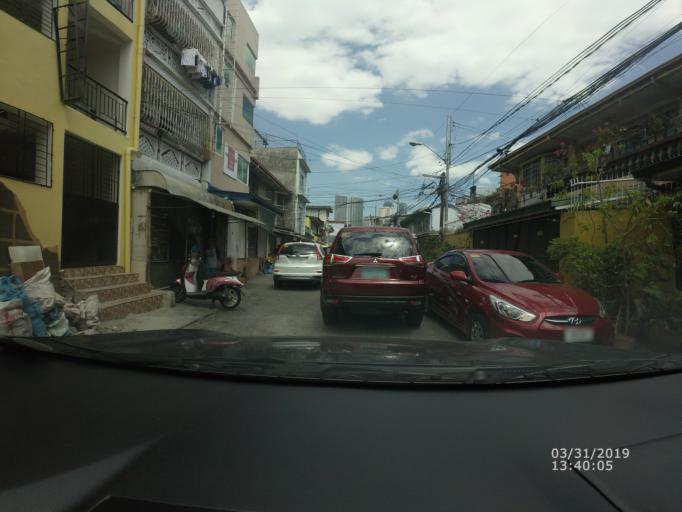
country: PH
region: Metro Manila
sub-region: Mandaluyong
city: Mandaluyong City
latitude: 14.5821
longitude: 121.0454
